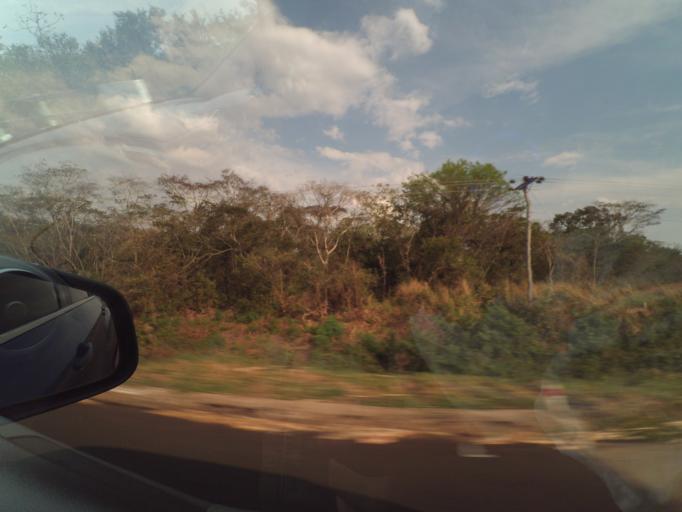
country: BO
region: Santa Cruz
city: Montero
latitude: -17.2713
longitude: -63.0947
